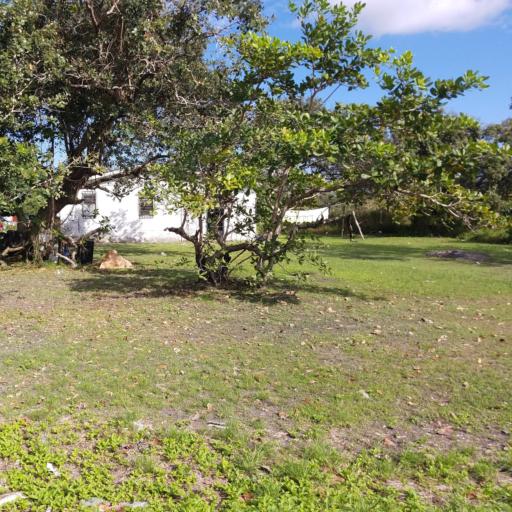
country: BZ
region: Belize
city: Belize City
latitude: 17.5644
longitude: -88.4116
